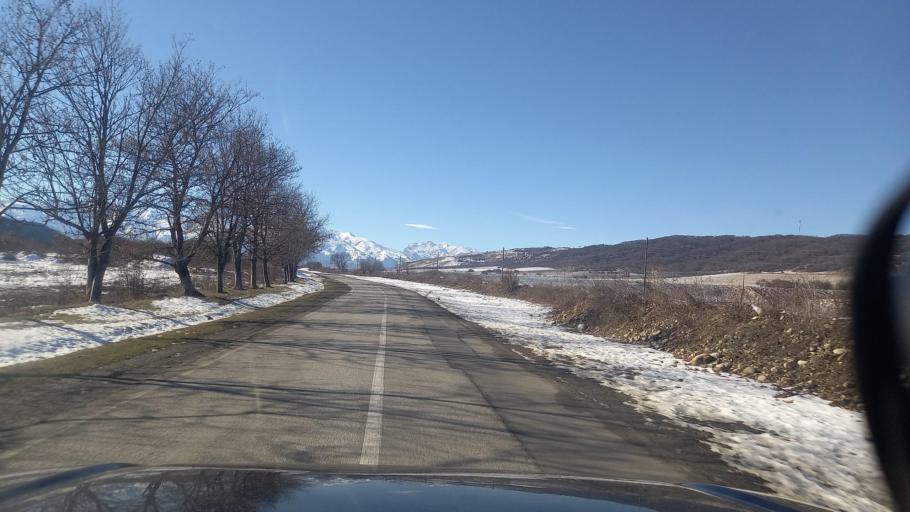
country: RU
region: North Ossetia
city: Chikola
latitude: 43.2477
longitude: 43.9657
